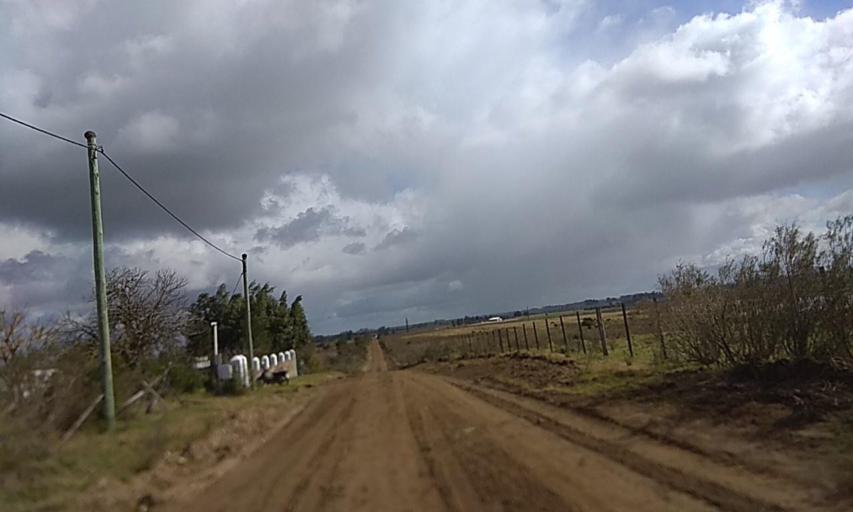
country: UY
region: Florida
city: Florida
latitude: -34.1136
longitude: -56.2342
